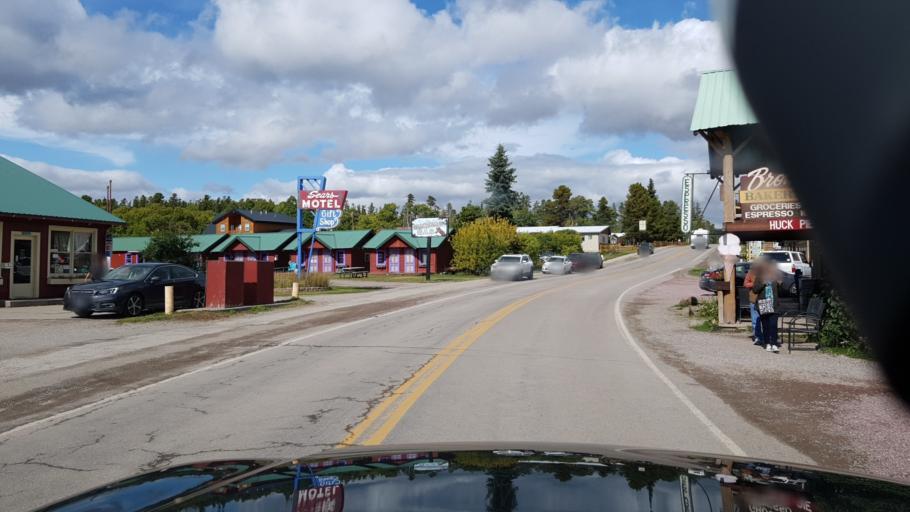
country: US
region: Montana
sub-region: Glacier County
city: South Browning
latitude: 48.4483
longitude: -113.2252
